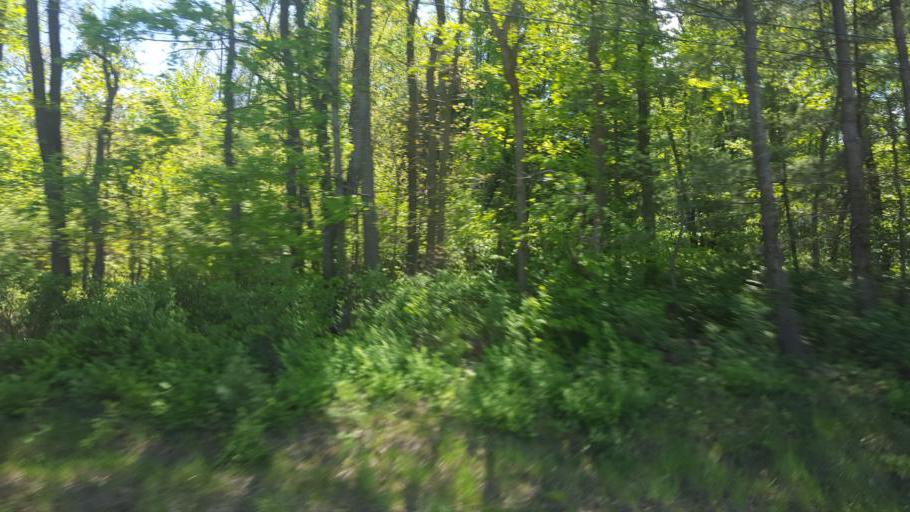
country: US
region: Ohio
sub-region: Knox County
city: Oak Hill
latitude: 40.2867
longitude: -82.2484
